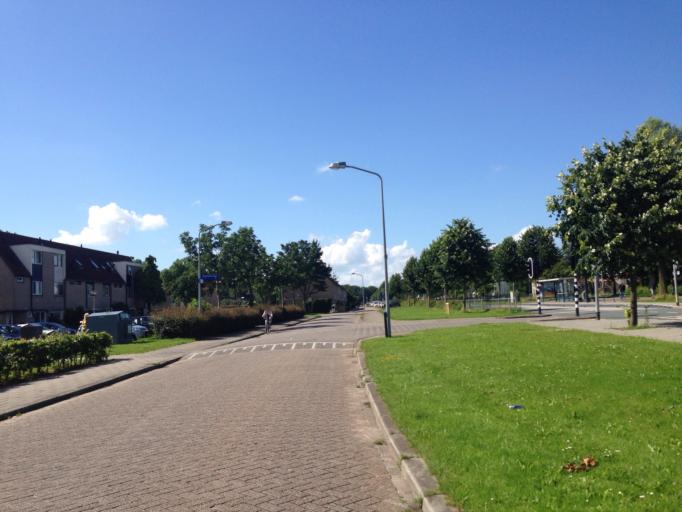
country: NL
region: Flevoland
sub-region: Gemeente Almere
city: Almere Stad
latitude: 52.3969
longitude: 5.2734
